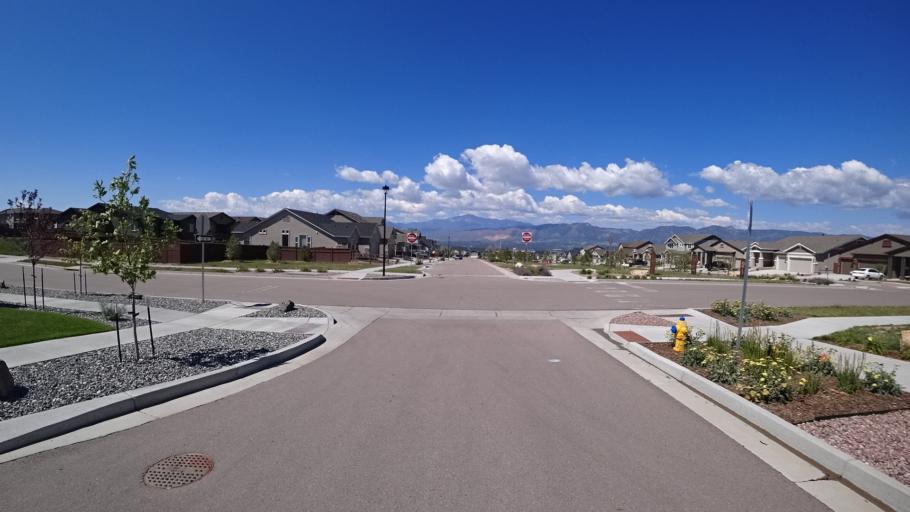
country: US
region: Colorado
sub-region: El Paso County
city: Black Forest
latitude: 38.9916
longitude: -104.7657
